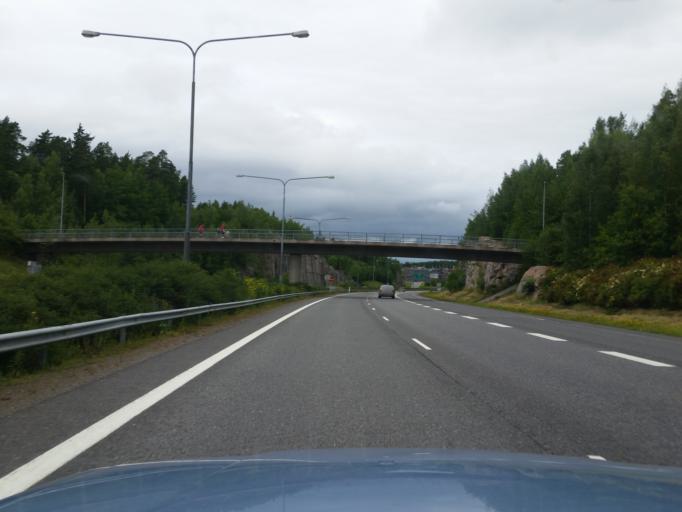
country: FI
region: Varsinais-Suomi
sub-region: Turku
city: Kaarina
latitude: 60.4246
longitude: 22.3363
